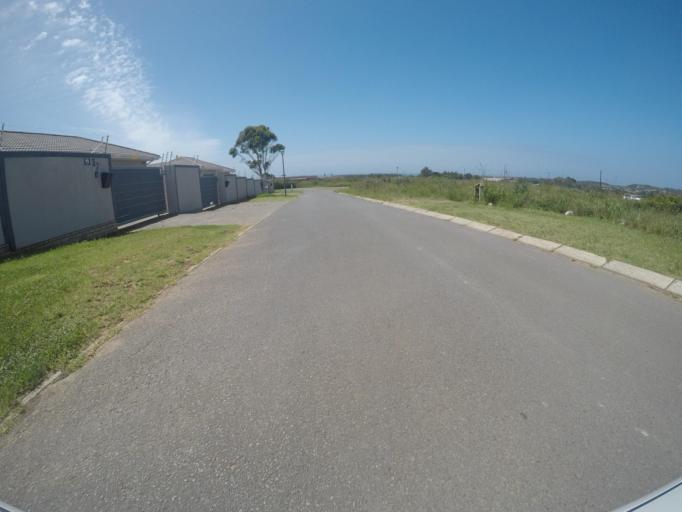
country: ZA
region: Eastern Cape
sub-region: Buffalo City Metropolitan Municipality
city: East London
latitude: -32.9440
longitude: 27.9944
